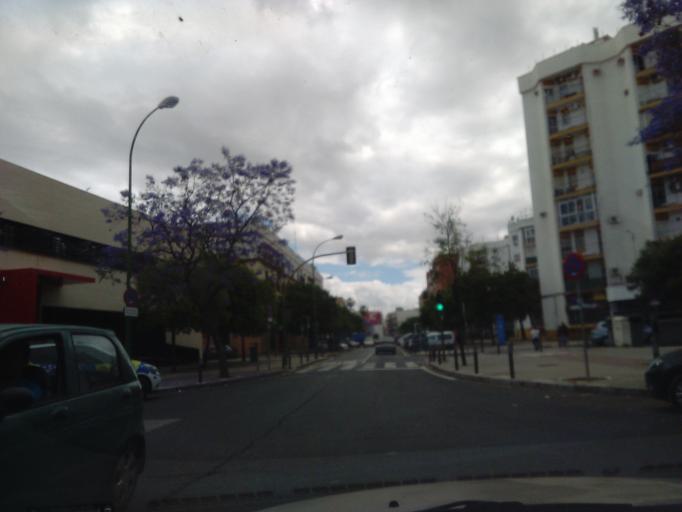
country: ES
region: Andalusia
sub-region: Provincia de Sevilla
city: Sevilla
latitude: 37.3729
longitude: -5.9526
